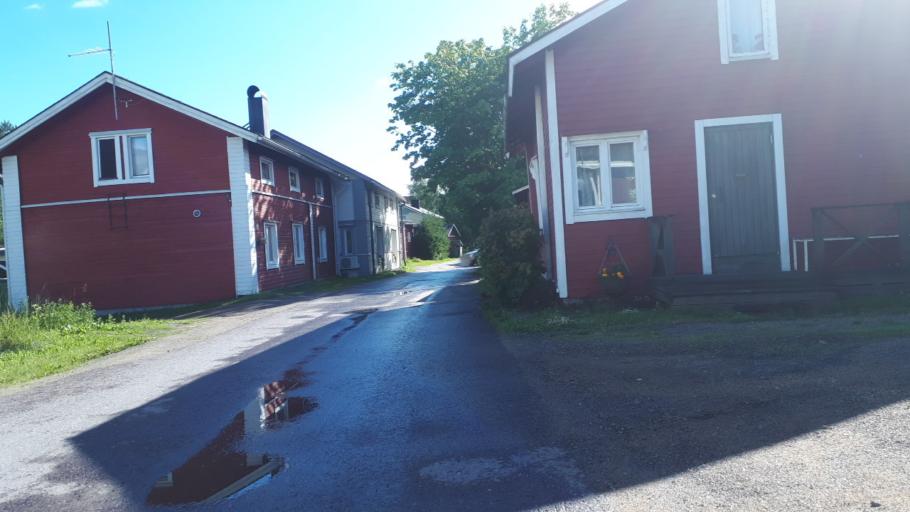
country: FI
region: Northern Ostrobothnia
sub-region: Oulunkaari
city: Ii
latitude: 65.3250
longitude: 25.3703
